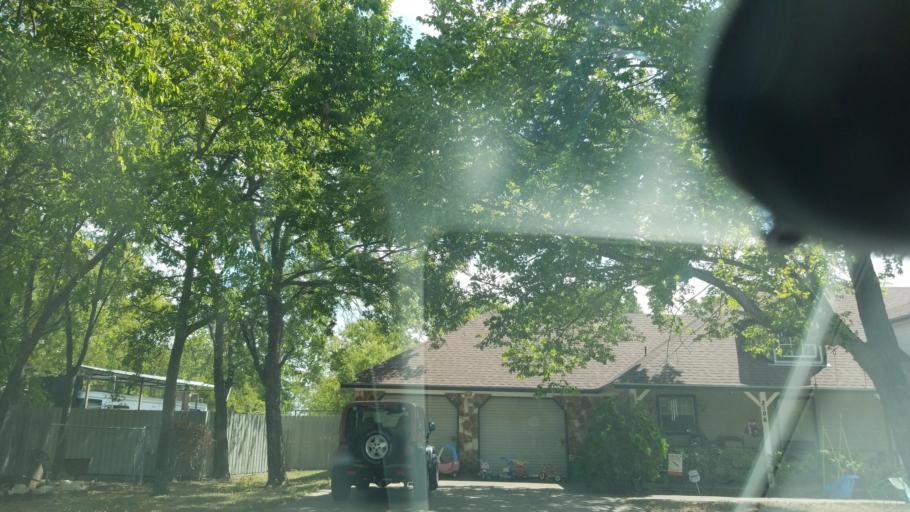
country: US
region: Texas
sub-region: Dallas County
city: Grand Prairie
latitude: 32.7184
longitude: -96.9909
